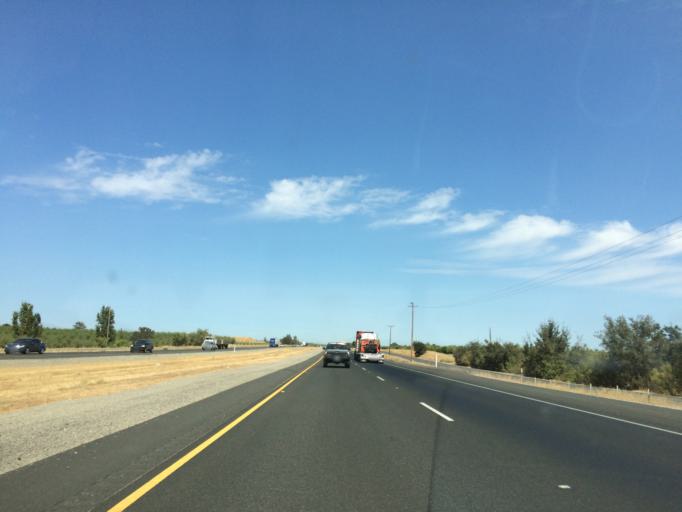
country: US
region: California
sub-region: Colusa County
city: Arbuckle
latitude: 38.9756
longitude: -122.0297
